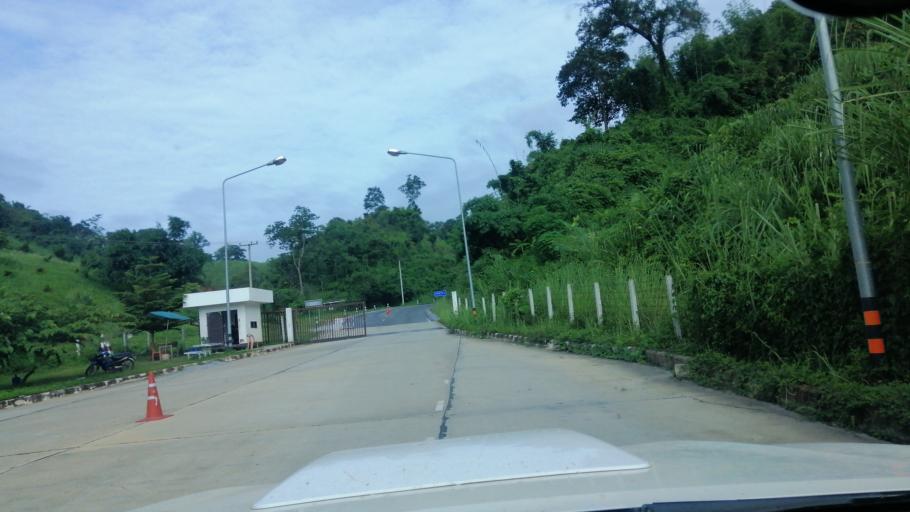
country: TH
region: Phayao
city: Phu Sang
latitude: 19.6766
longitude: 100.4357
